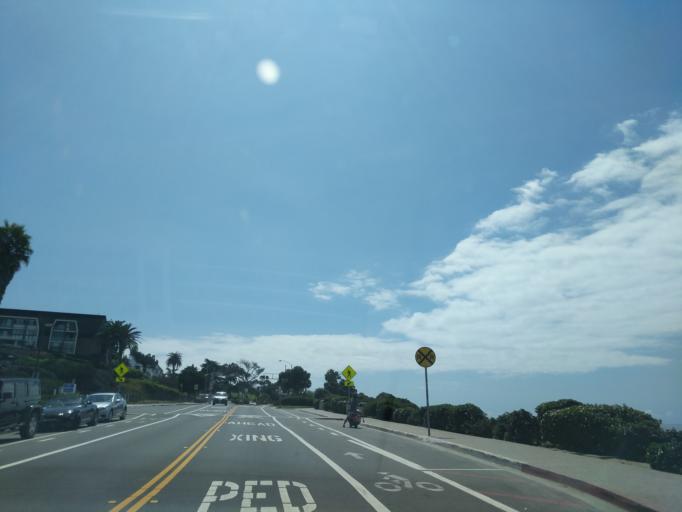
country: US
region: California
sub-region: San Diego County
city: Del Mar
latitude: 32.9614
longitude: -117.2677
